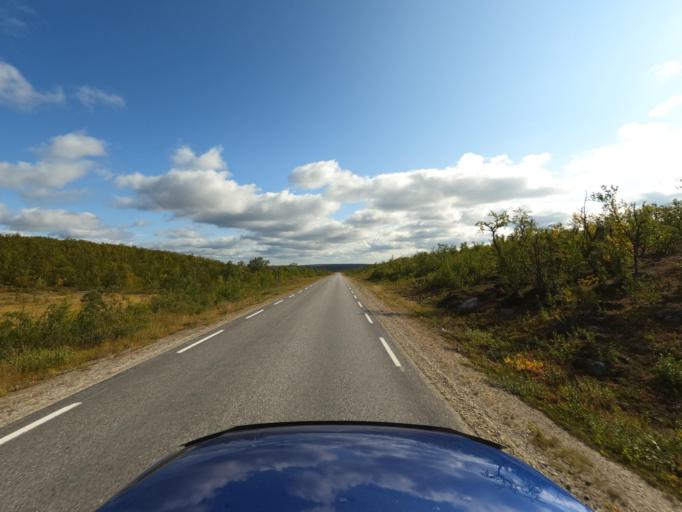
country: NO
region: Finnmark Fylke
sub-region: Porsanger
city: Lakselv
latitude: 69.3941
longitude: 24.5645
